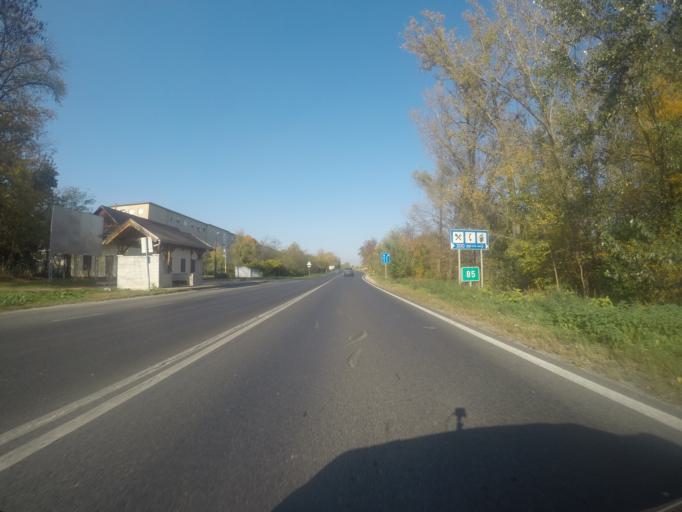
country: HU
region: Tolna
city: Dunafoldvar
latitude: 46.8318
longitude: 18.9085
